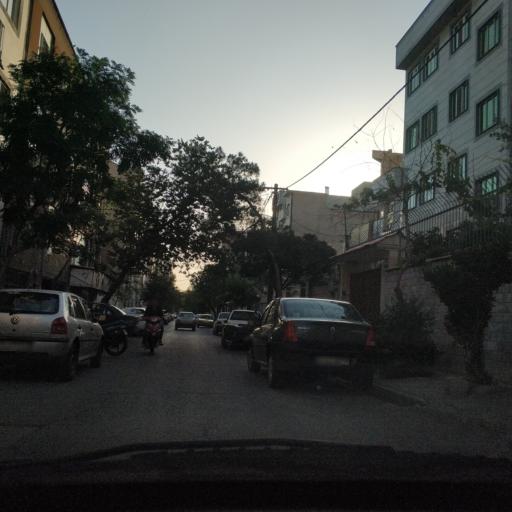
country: IR
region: Tehran
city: Tehran
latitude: 35.7171
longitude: 51.4769
